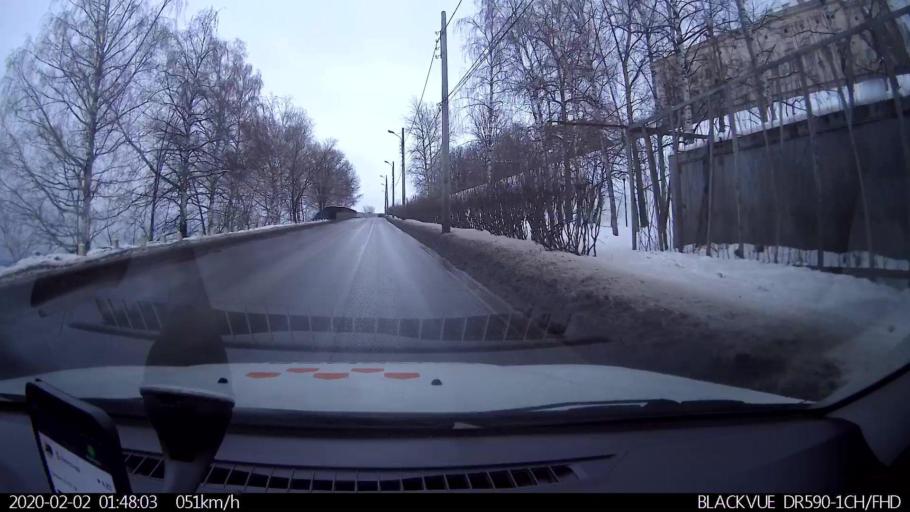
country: RU
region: Nizjnij Novgorod
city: Nizhniy Novgorod
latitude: 56.3311
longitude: 44.0353
